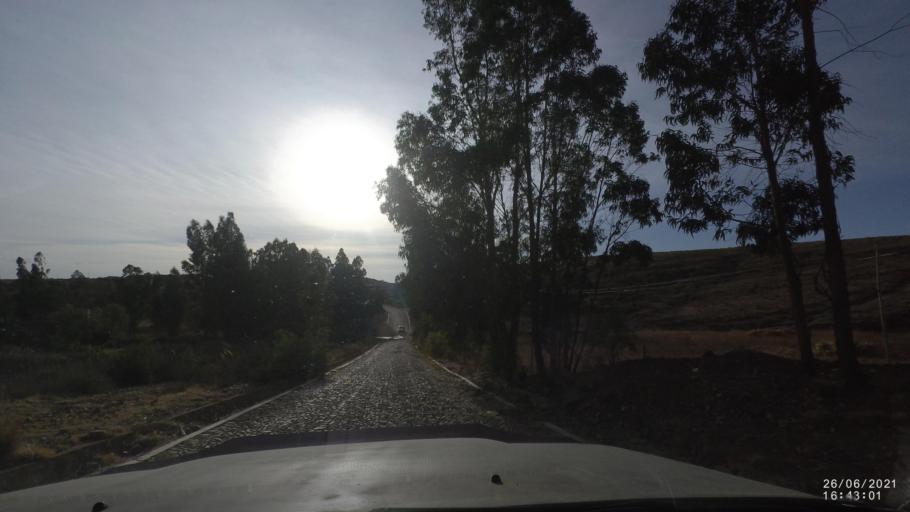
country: BO
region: Cochabamba
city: Cliza
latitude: -17.7604
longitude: -65.8299
